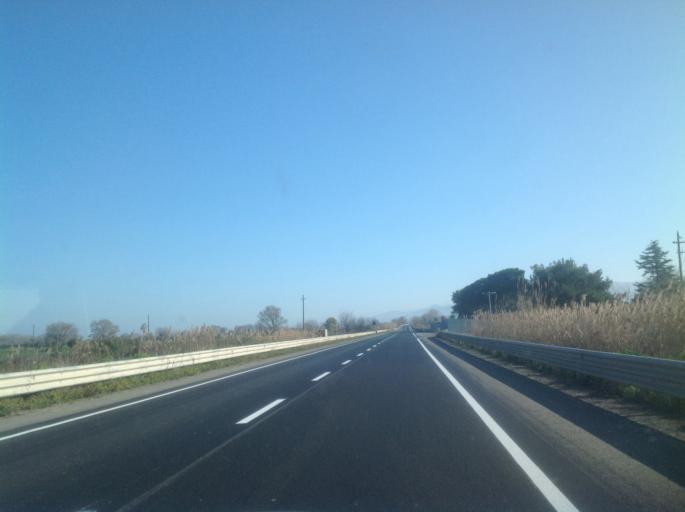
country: IT
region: Calabria
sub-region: Provincia di Cosenza
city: Sibari
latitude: 39.7193
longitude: 16.4904
